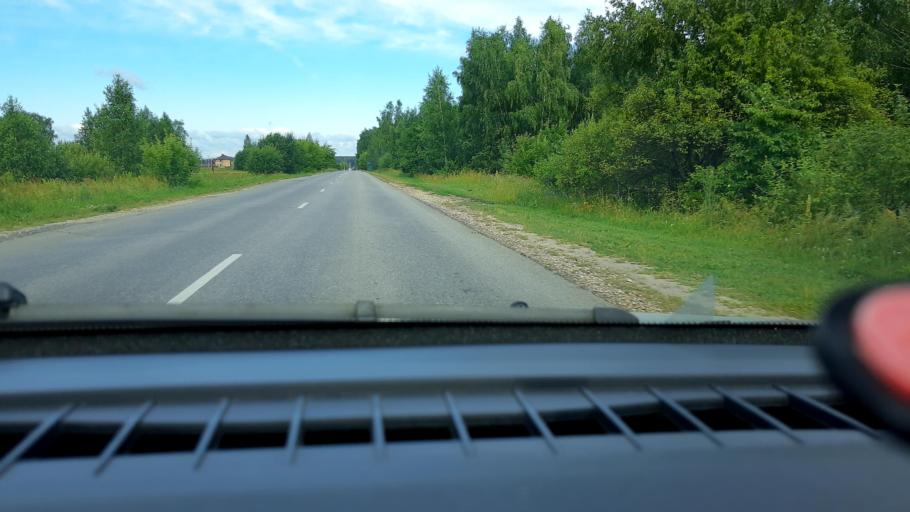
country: RU
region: Nizjnij Novgorod
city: Kstovo
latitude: 56.1523
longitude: 44.2865
